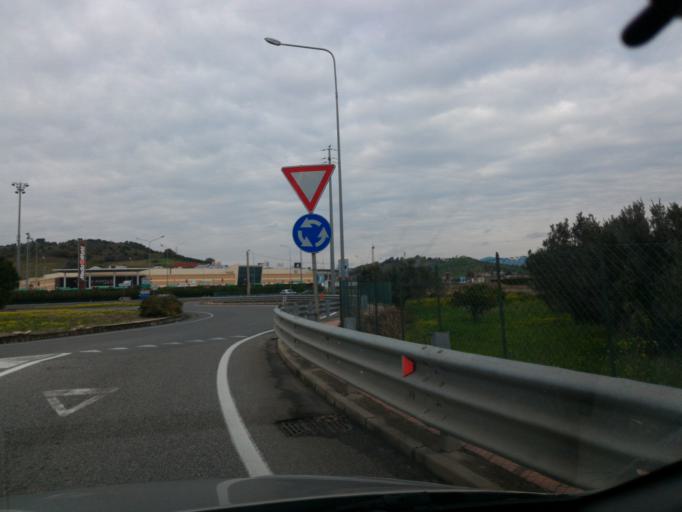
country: IT
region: Calabria
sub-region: Provincia di Catanzaro
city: Barone
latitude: 38.8431
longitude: 16.6501
